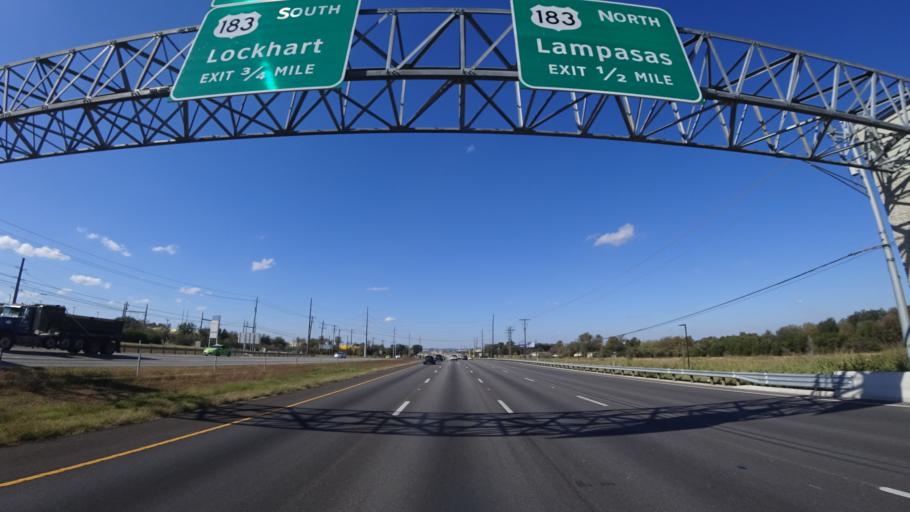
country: US
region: Texas
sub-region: Travis County
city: Austin
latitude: 30.2193
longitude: -97.6703
